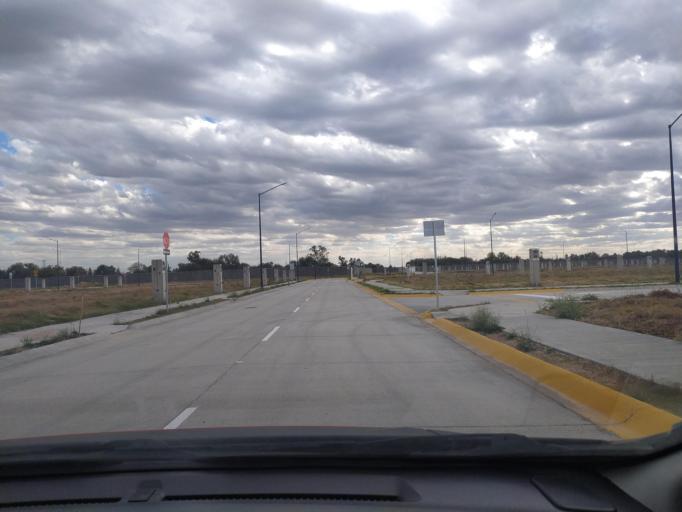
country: LA
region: Oudomxai
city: Muang La
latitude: 21.0251
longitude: 101.8220
